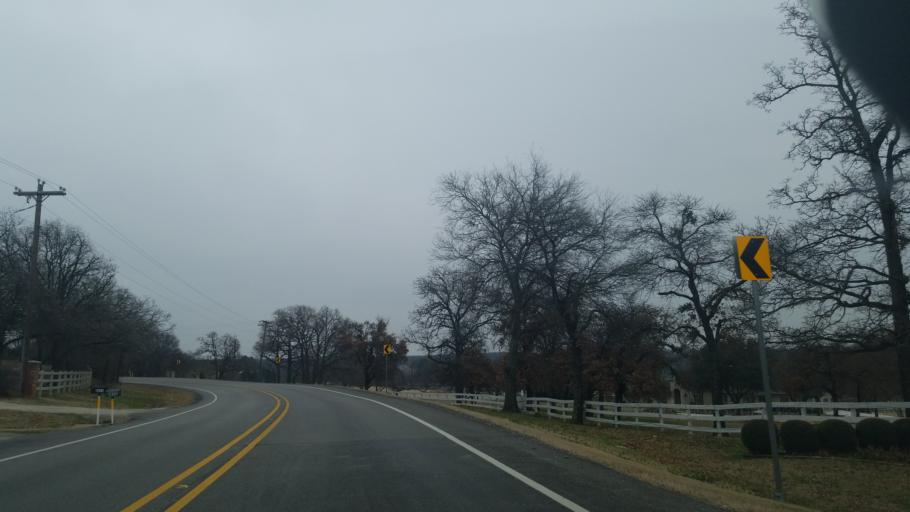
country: US
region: Texas
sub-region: Denton County
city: Argyle
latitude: 33.1303
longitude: -97.1440
